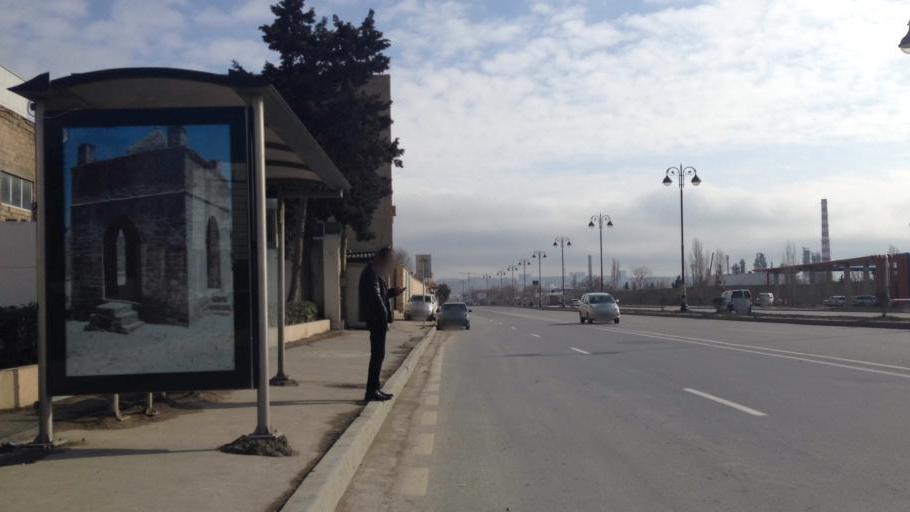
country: AZ
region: Baki
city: Baku
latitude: 40.3778
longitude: 49.8972
